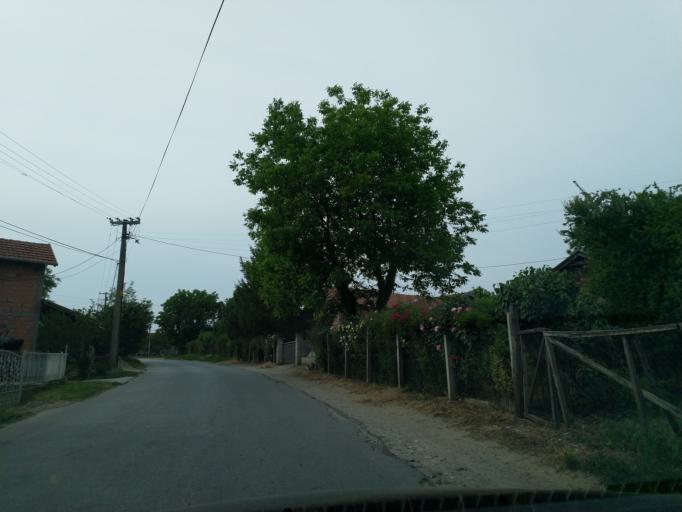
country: RS
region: Central Serbia
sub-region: Pomoravski Okrug
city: Jagodina
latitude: 43.9696
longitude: 21.2273
